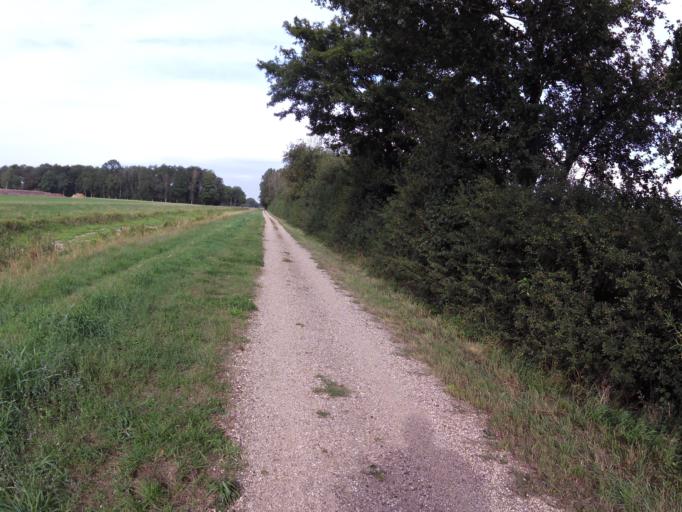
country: NL
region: Gelderland
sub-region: Oude IJsselstreek
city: Varsseveld
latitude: 51.9440
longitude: 6.5034
